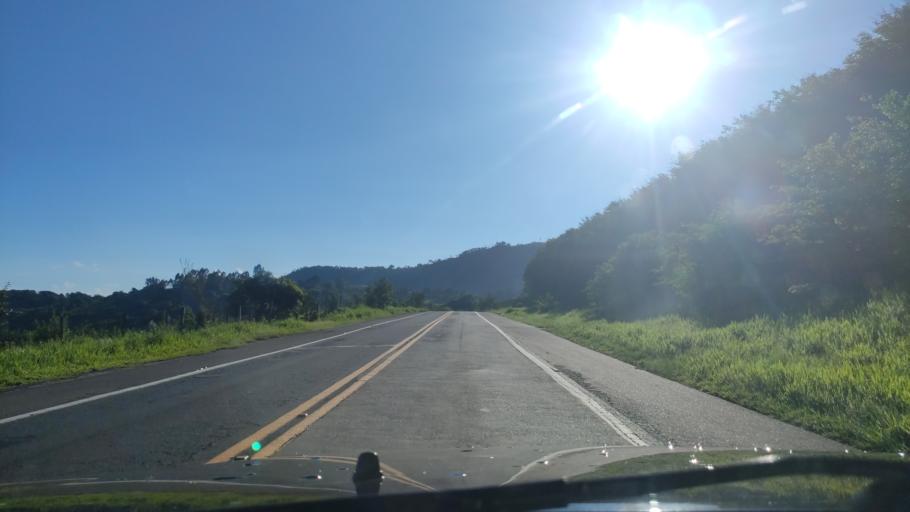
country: BR
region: Sao Paulo
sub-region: Socorro
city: Socorro
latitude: -22.5583
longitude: -46.6009
